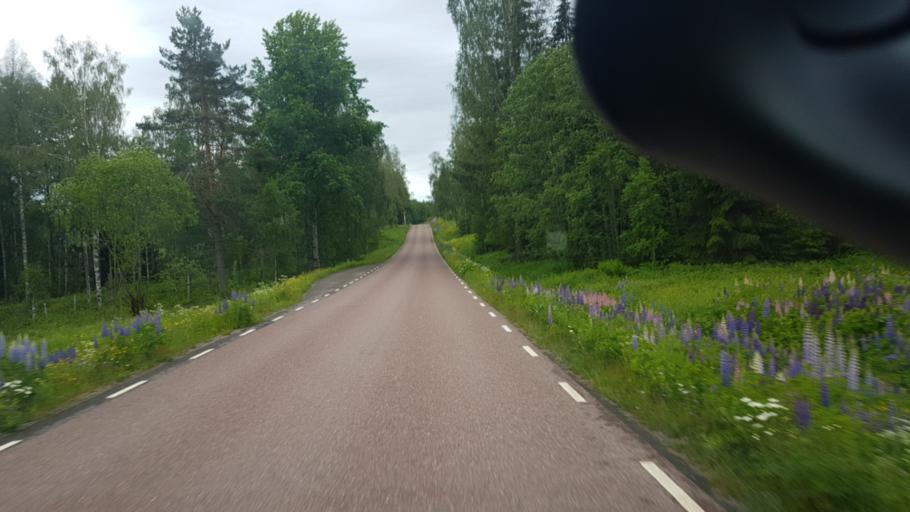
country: NO
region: Ostfold
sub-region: Romskog
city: Romskog
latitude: 59.7316
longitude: 12.0632
